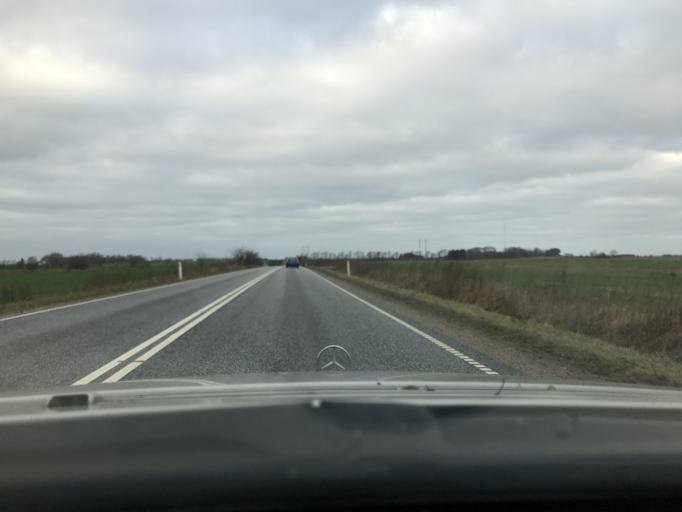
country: DK
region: South Denmark
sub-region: Aabenraa Kommune
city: Rodekro
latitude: 55.0953
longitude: 9.1940
